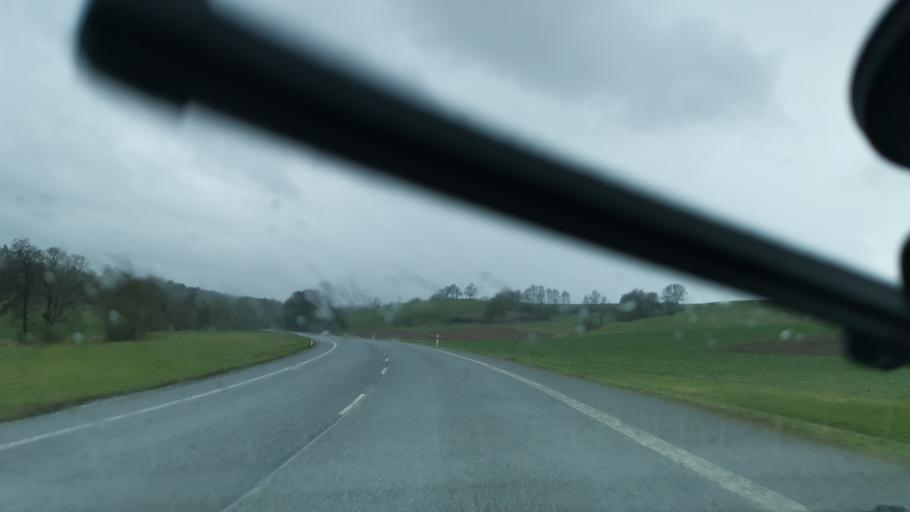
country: DE
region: Hesse
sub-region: Regierungsbezirk Kassel
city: Cornberg
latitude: 51.0543
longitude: 9.8792
